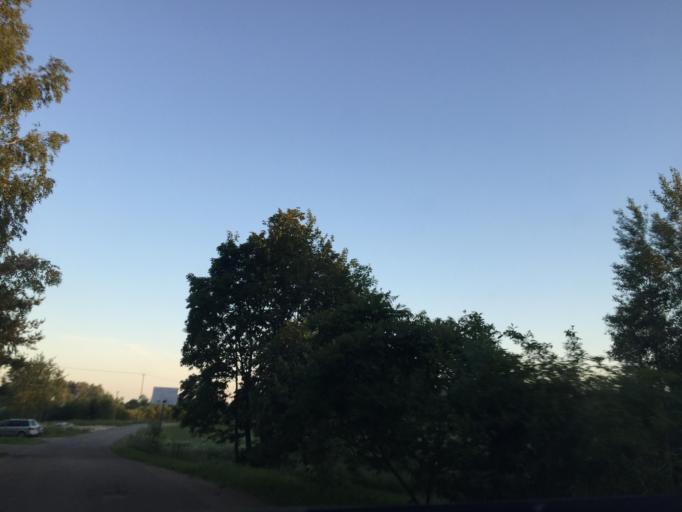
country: LV
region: Rezekne
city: Rezekne
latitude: 56.3794
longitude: 27.4148
